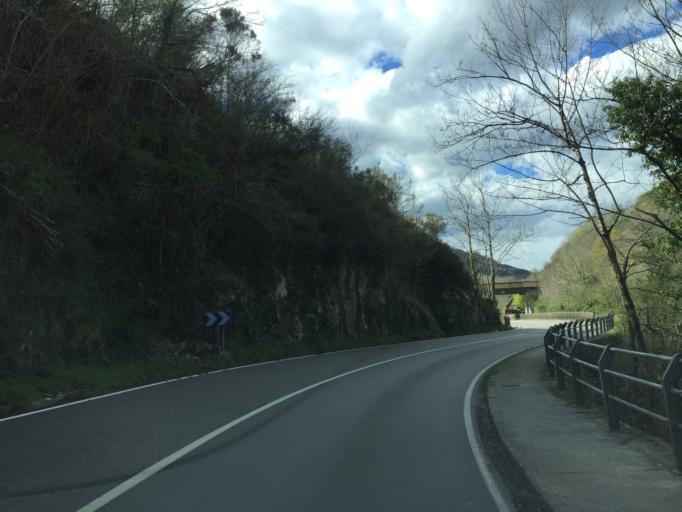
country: ES
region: Asturias
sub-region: Province of Asturias
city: Amieva
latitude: 43.3139
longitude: -5.0668
